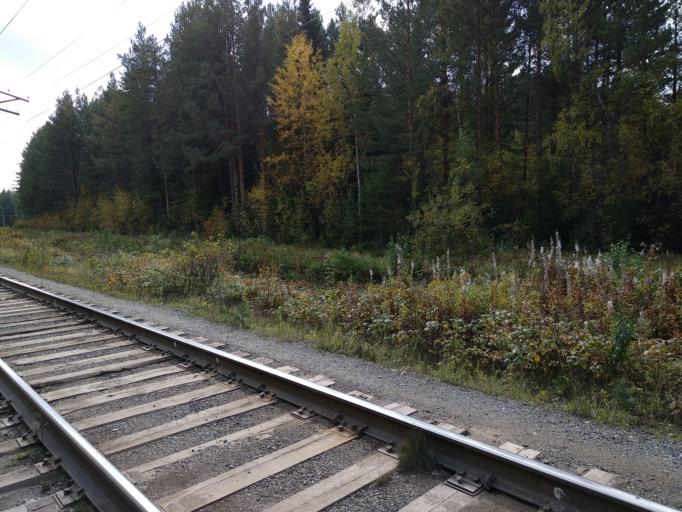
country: RU
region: Sverdlovsk
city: Krasnotur'insk
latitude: 59.7530
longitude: 60.1624
